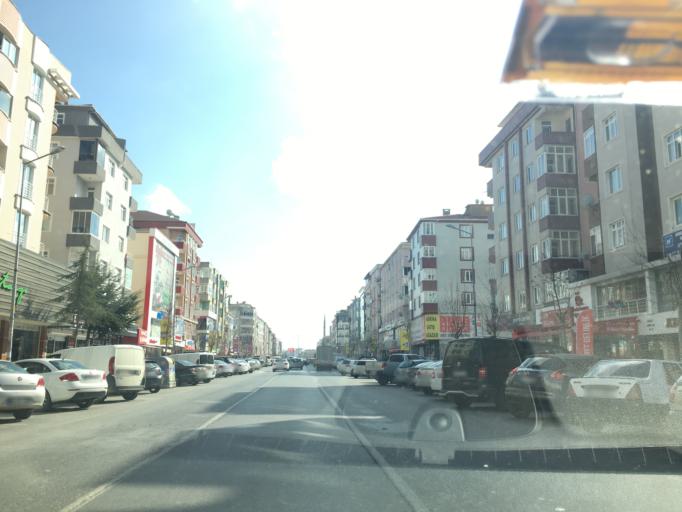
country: TR
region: Tekirdag
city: Cerkezkoey
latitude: 41.2918
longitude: 27.9983
